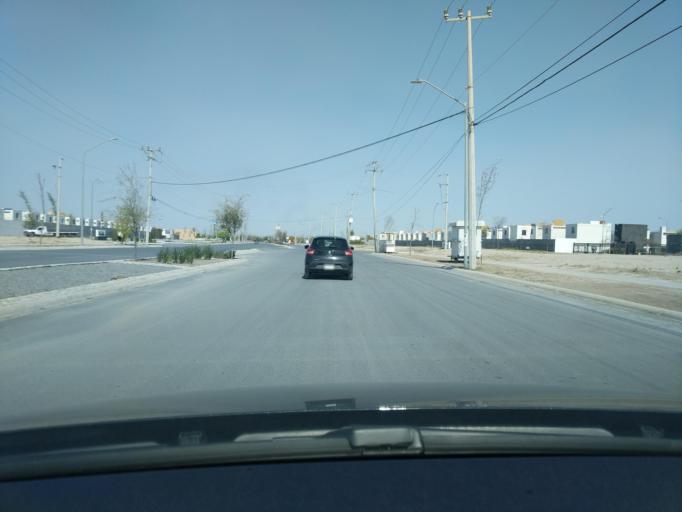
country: MX
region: Nuevo Leon
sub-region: Garcia
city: Los Parques
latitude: 25.7822
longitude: -100.4896
